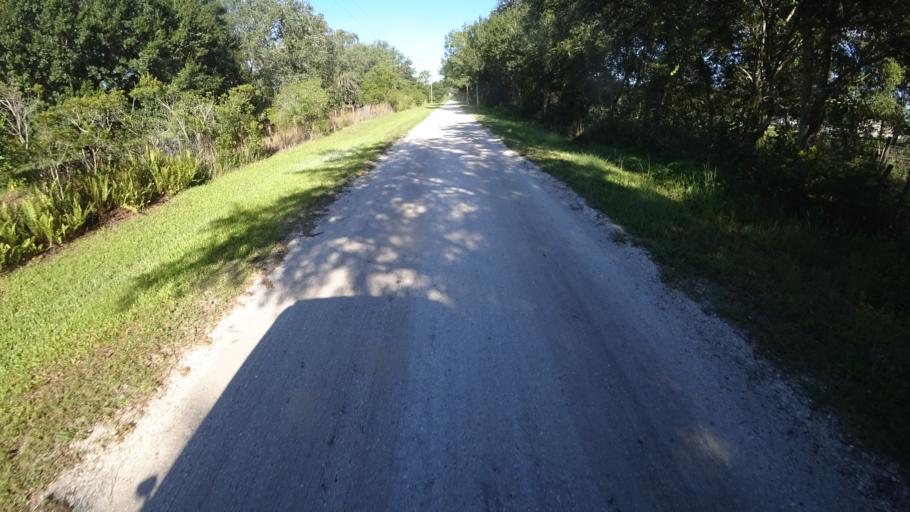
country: US
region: Florida
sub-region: Sarasota County
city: The Meadows
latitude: 27.4193
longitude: -82.2579
